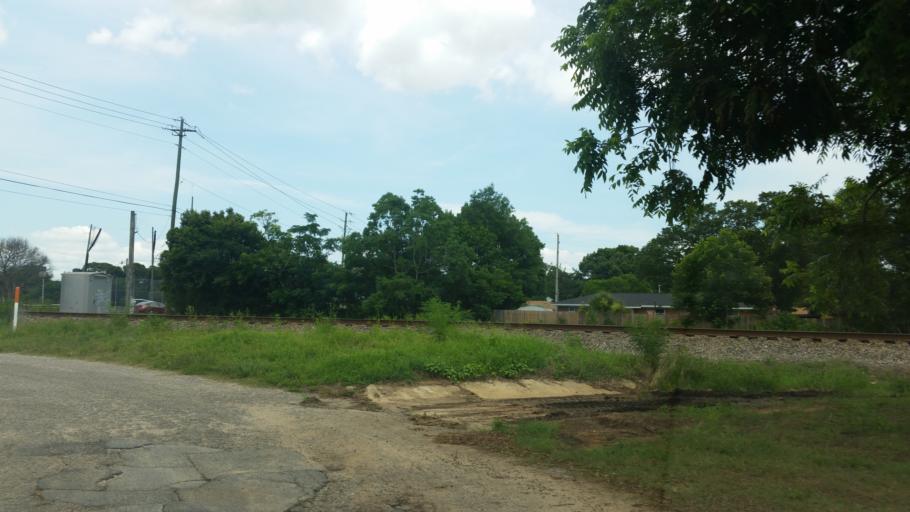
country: US
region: Florida
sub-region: Escambia County
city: Brent
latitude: 30.4770
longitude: -87.2410
